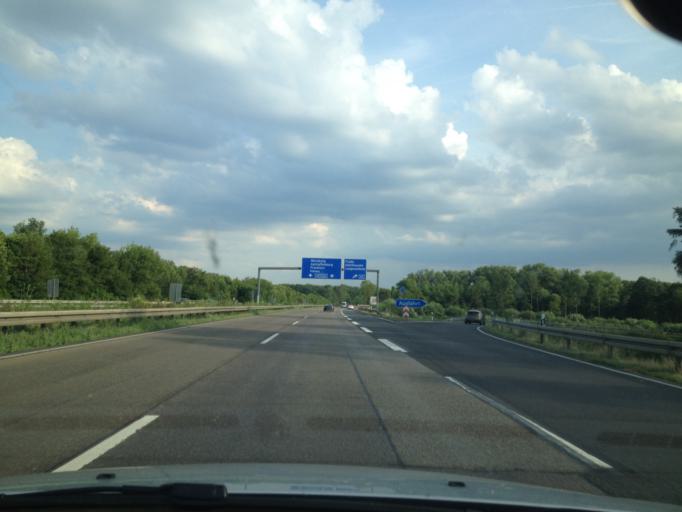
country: DE
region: Hesse
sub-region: Regierungsbezirk Darmstadt
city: Langenselbold
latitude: 50.1688
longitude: 9.0172
